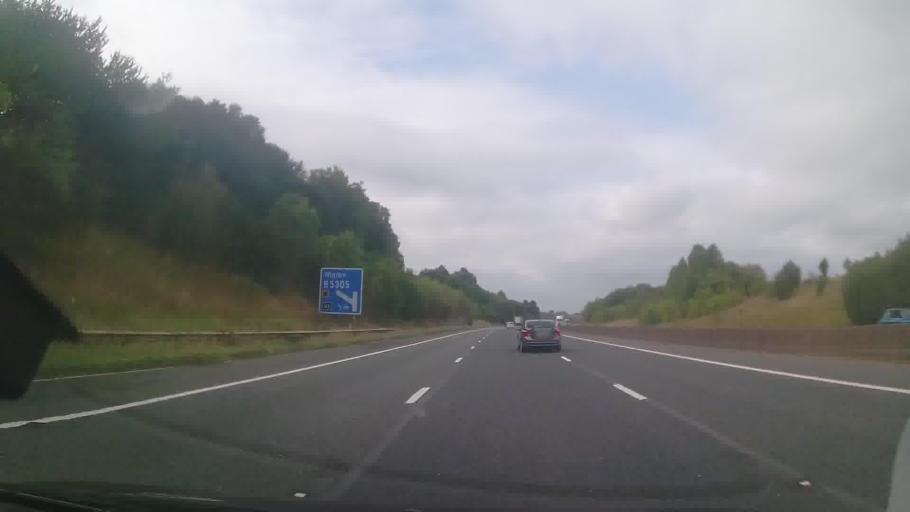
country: GB
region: England
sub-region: Cumbria
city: Penrith
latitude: 54.6793
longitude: -2.7855
